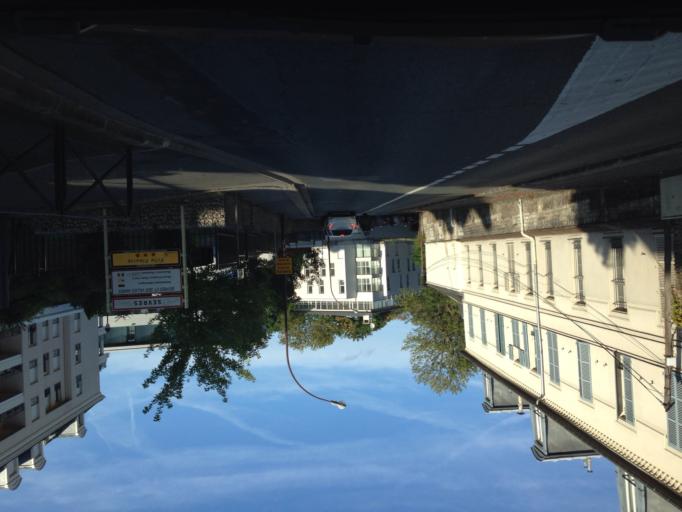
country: FR
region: Ile-de-France
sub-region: Departement des Hauts-de-Seine
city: Sevres
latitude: 48.8228
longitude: 2.2253
